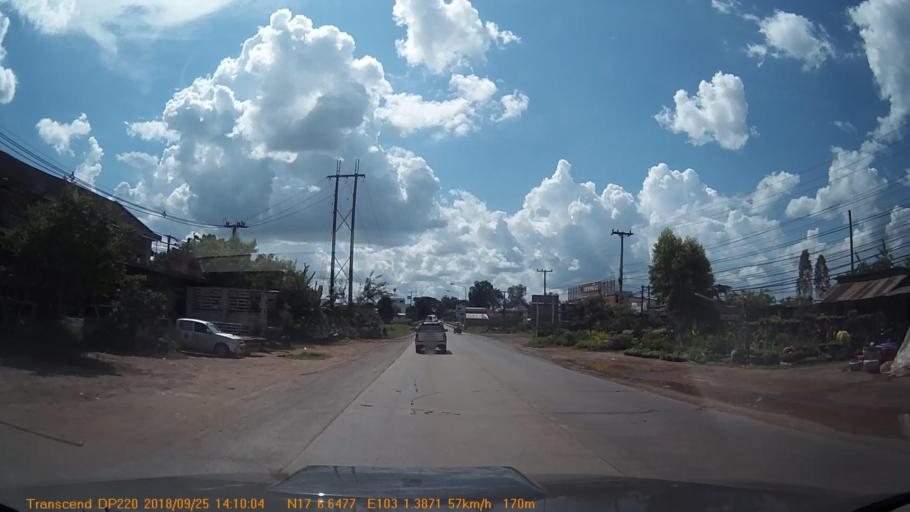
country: TH
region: Changwat Udon Thani
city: Kumphawapi
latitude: 17.1108
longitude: 103.0229
